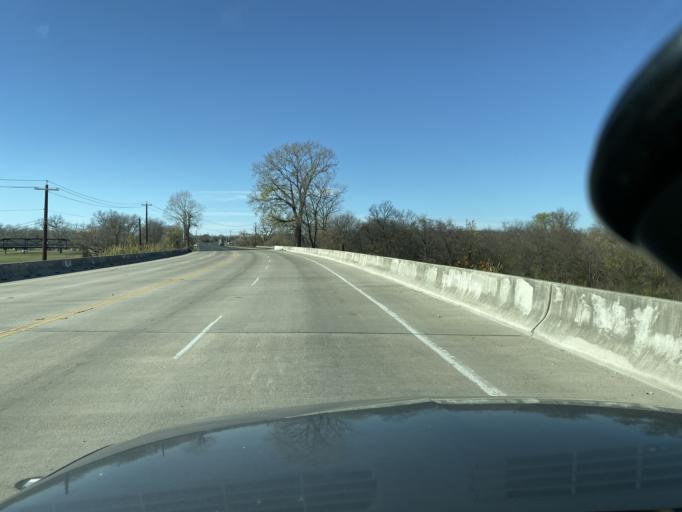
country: US
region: Texas
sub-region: Travis County
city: Garfield
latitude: 30.1696
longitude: -97.6617
